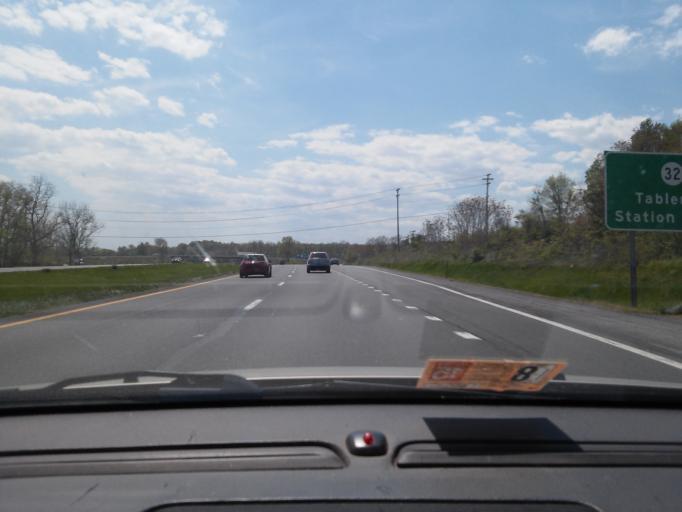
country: US
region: West Virginia
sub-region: Berkeley County
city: Inwood
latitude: 39.4105
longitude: -78.0201
